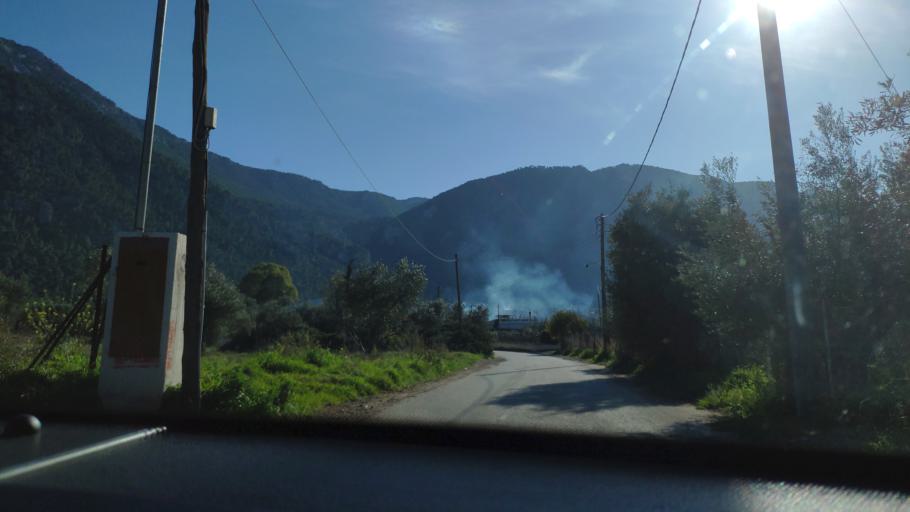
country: GR
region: Peloponnese
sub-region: Nomos Korinthias
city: Perachora
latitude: 38.0486
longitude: 23.0329
